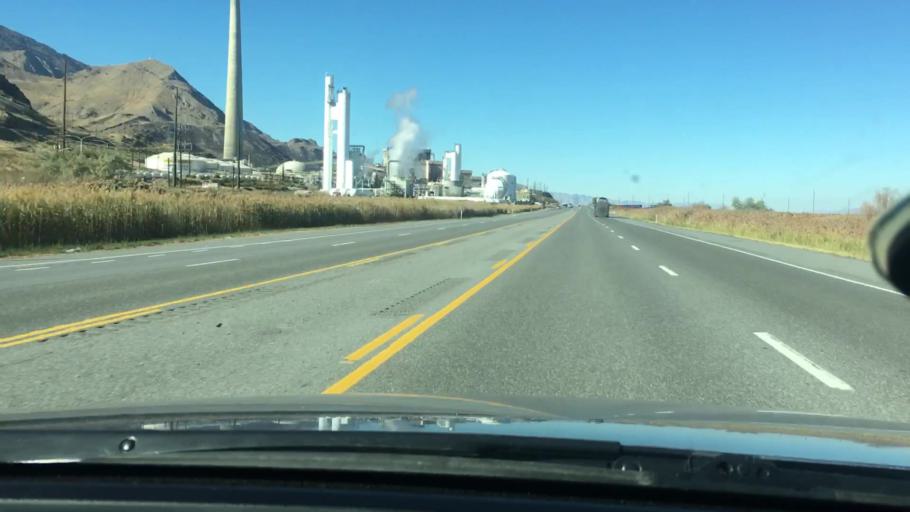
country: US
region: Utah
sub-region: Salt Lake County
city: Magna
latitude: 40.7277
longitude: -112.1805
